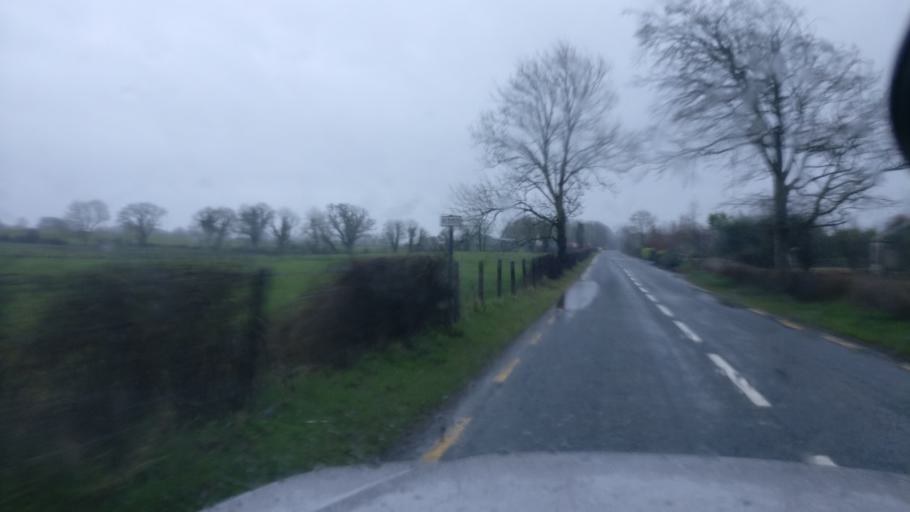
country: IE
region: Connaught
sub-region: County Galway
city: Ballinasloe
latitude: 53.2659
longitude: -8.1930
